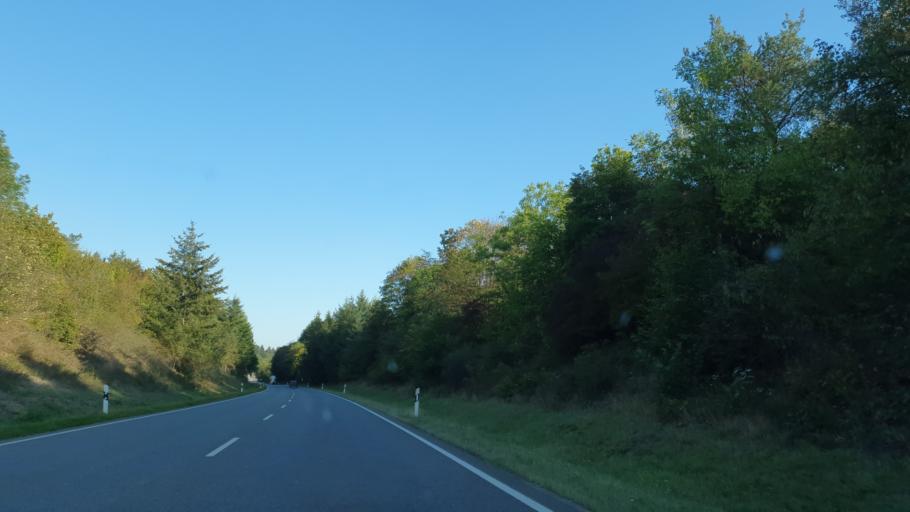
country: DE
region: Rheinland-Pfalz
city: Nortershausen
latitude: 50.2233
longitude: 7.5238
